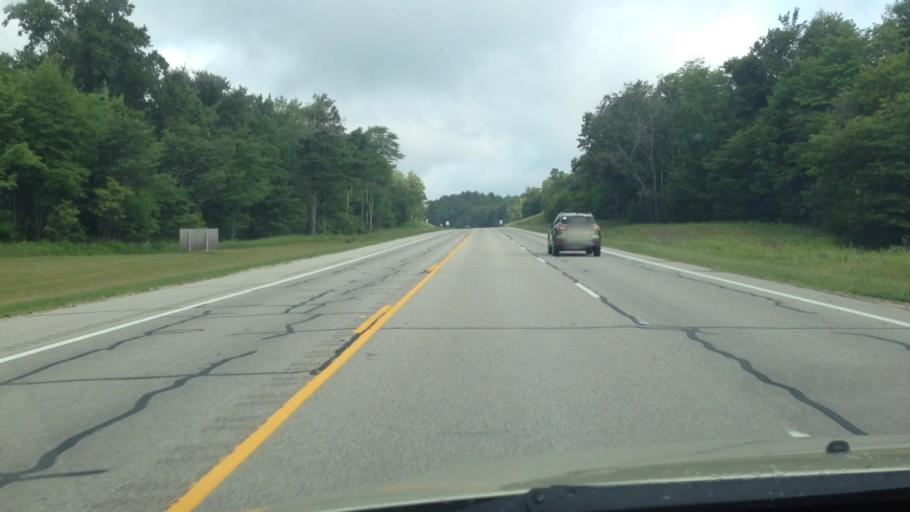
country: US
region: Michigan
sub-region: Mackinac County
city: Saint Ignace
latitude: 46.0125
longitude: -85.0129
